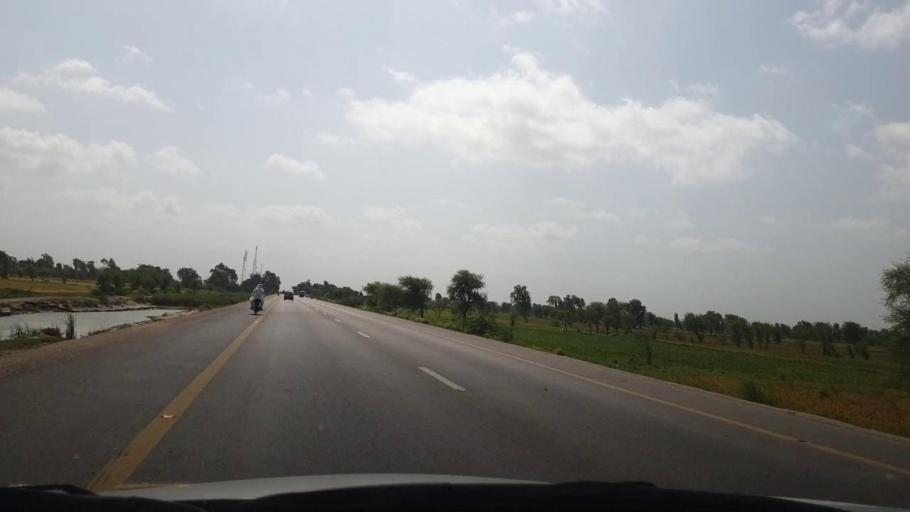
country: PK
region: Sindh
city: Matli
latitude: 24.9460
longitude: 68.6987
